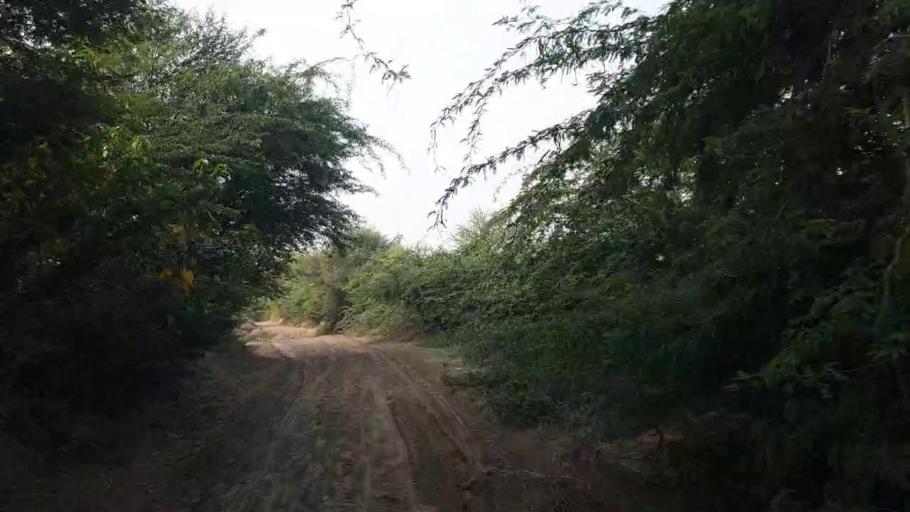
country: PK
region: Sindh
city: Tando Bago
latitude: 24.7814
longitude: 68.8777
